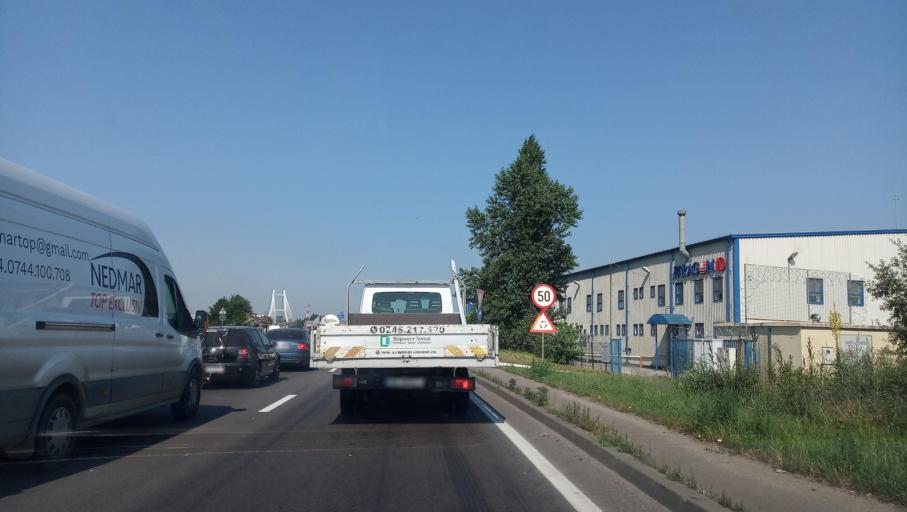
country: RO
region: Ilfov
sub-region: Comuna Otopeni
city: Otopeni
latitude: 44.5383
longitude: 26.0859
